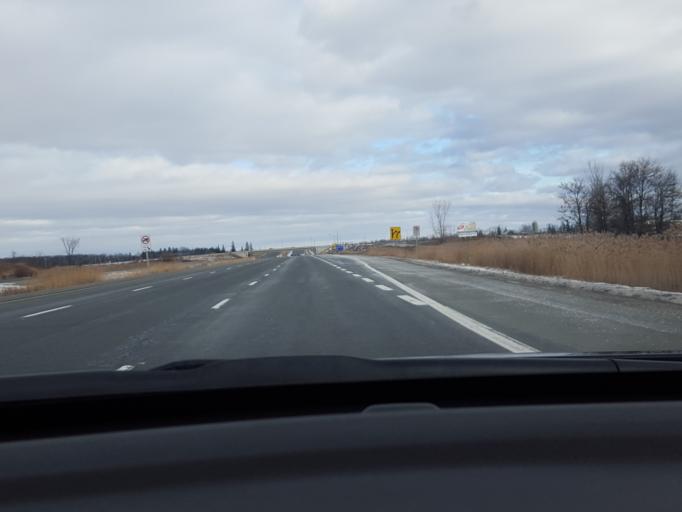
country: CA
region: Ontario
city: Markham
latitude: 43.8722
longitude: -79.2242
